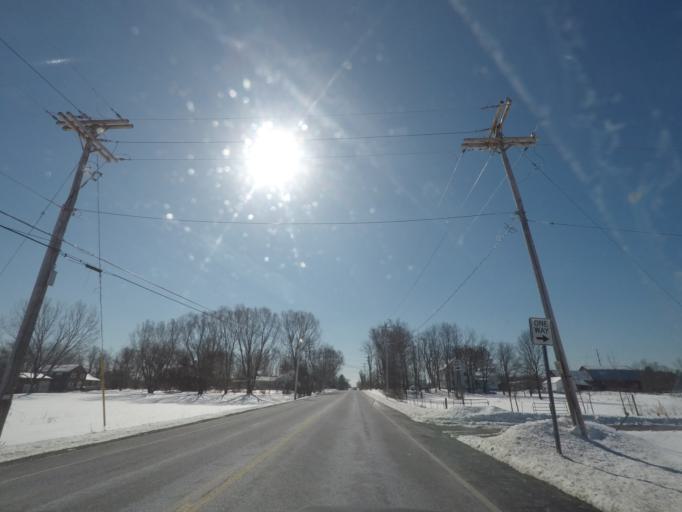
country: US
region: New York
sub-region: Saratoga County
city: Ballston Spa
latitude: 42.9608
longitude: -73.8293
